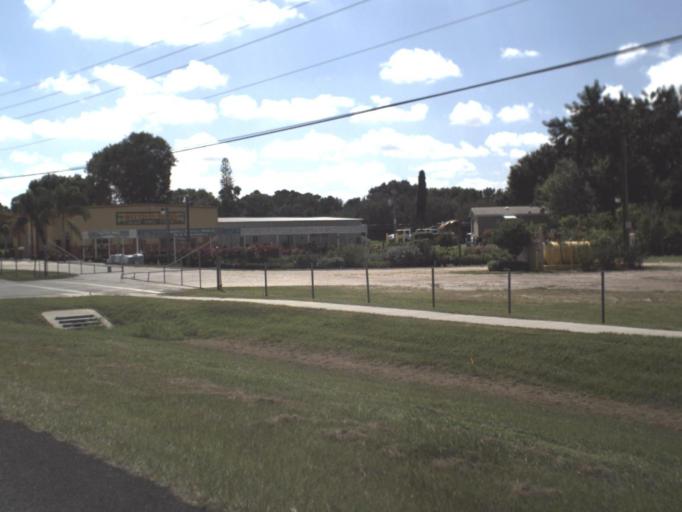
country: US
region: Florida
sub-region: Lee County
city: San Carlos Park
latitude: 26.4577
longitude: -81.8258
